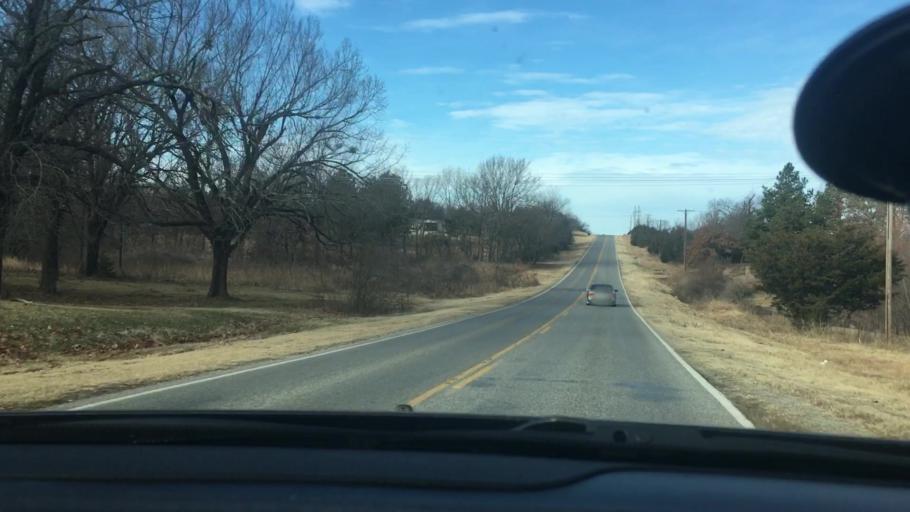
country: US
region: Oklahoma
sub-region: Seminole County
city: Konawa
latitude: 34.9463
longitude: -96.7297
